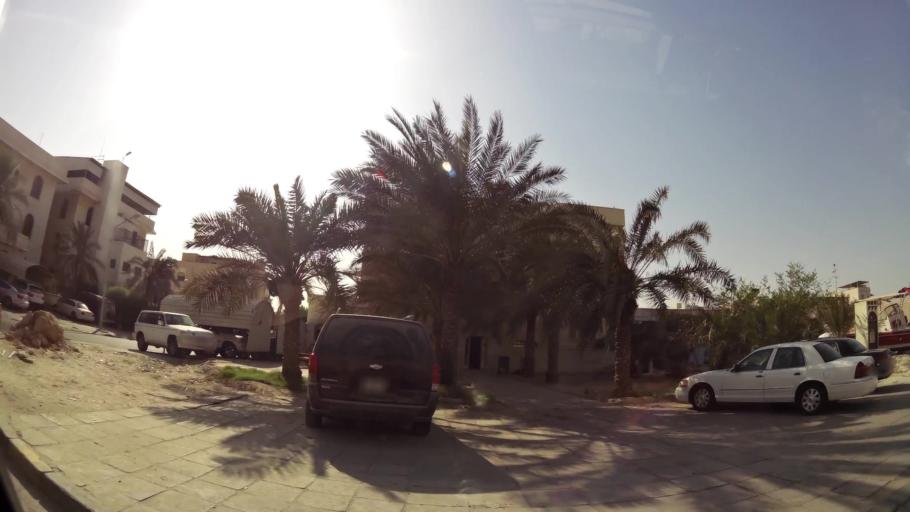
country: KW
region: Muhafazat Hawalli
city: Salwa
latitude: 29.2940
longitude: 48.0769
